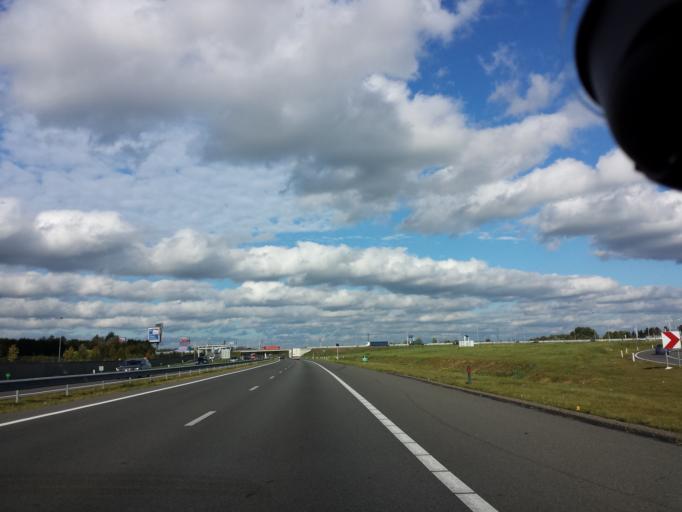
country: NL
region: Limburg
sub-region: Gemeente Roermond
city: Leeuwen
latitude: 51.2042
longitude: 6.0271
